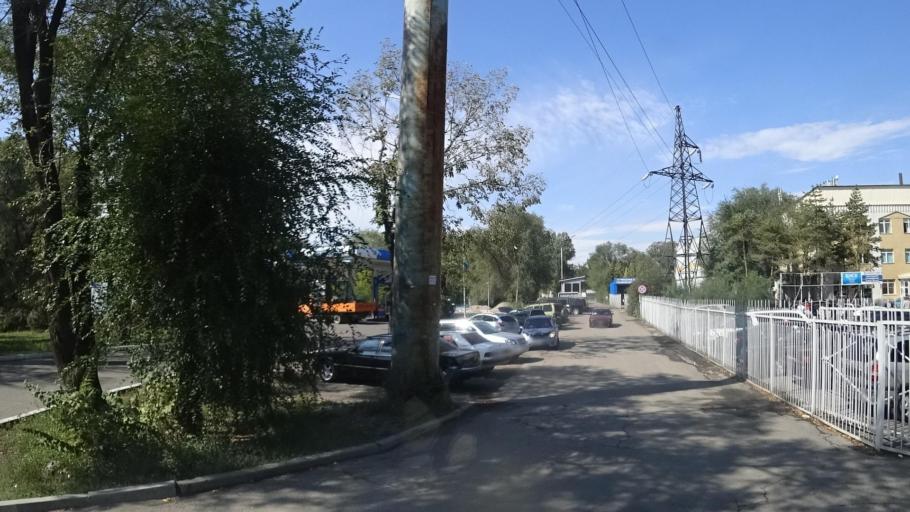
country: KZ
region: Almaty Oblysy
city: Pervomayskiy
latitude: 43.3331
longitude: 76.9790
